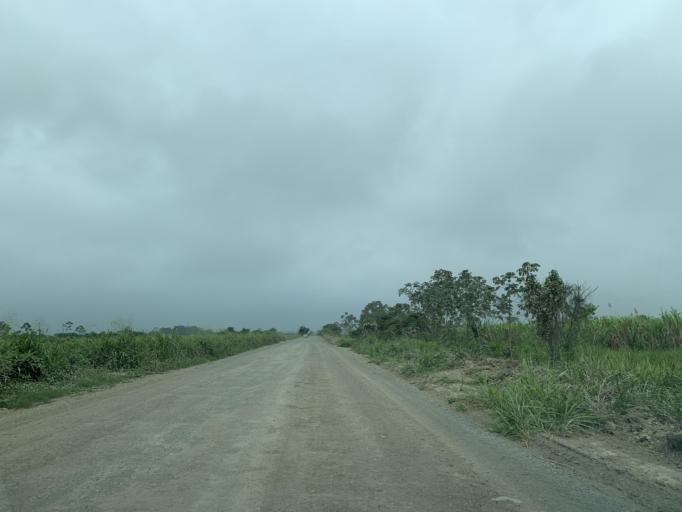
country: EC
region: Guayas
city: Coronel Marcelino Mariduena
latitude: -2.3597
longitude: -79.5487
